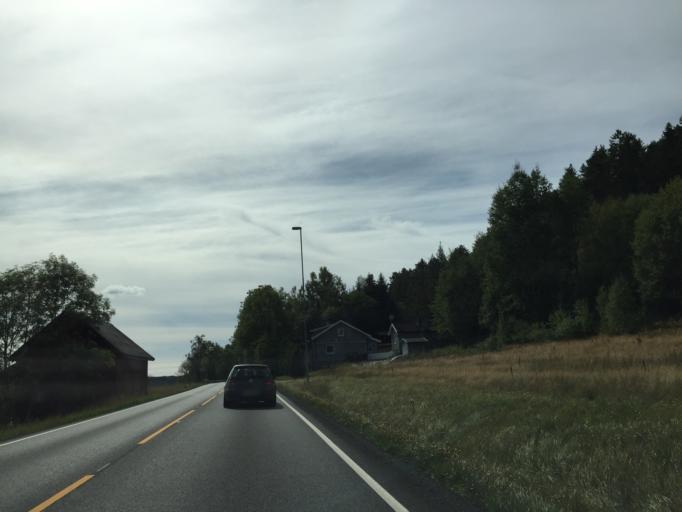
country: NO
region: Ostfold
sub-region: Fredrikstad
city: Fredrikstad
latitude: 59.2827
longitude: 10.9010
